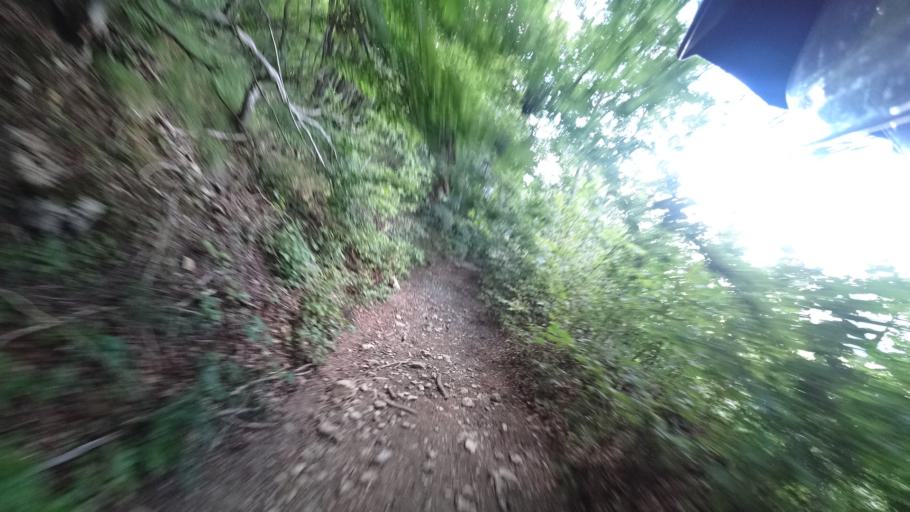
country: HR
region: Zadarska
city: Gracac
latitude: 44.3655
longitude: 16.0853
